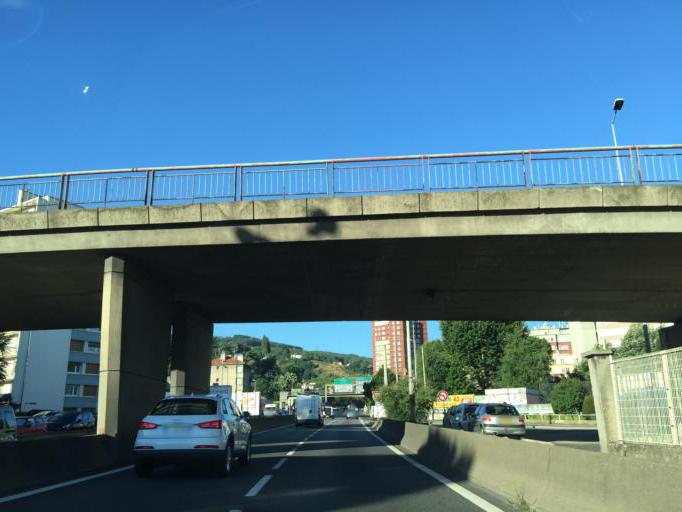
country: FR
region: Rhone-Alpes
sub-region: Departement de la Loire
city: Saint-Etienne
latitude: 45.4140
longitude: 4.4027
